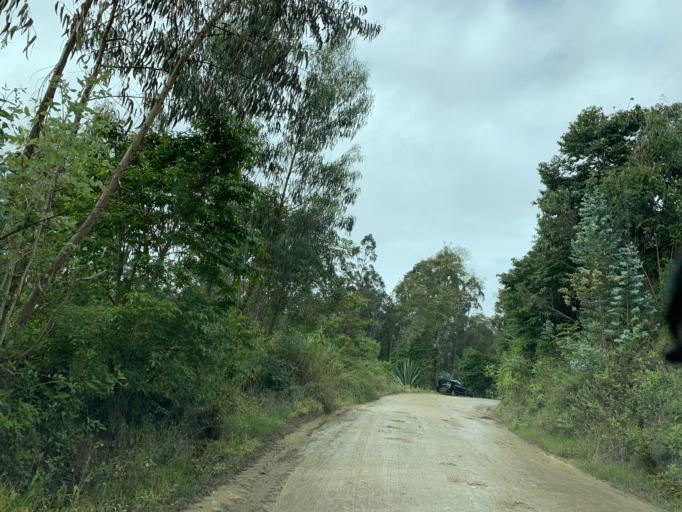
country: CO
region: Boyaca
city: Tibana
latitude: 5.3146
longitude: -73.4228
